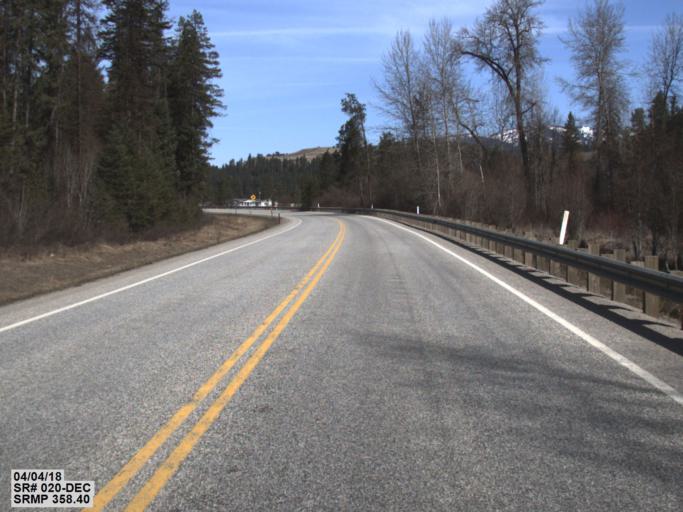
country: US
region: Washington
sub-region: Stevens County
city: Colville
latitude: 48.5370
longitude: -117.8235
